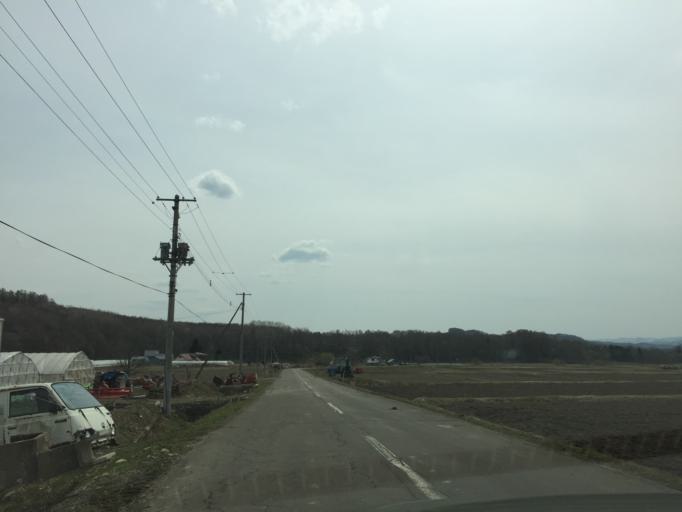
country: JP
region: Hokkaido
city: Ashibetsu
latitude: 43.6177
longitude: 142.2150
